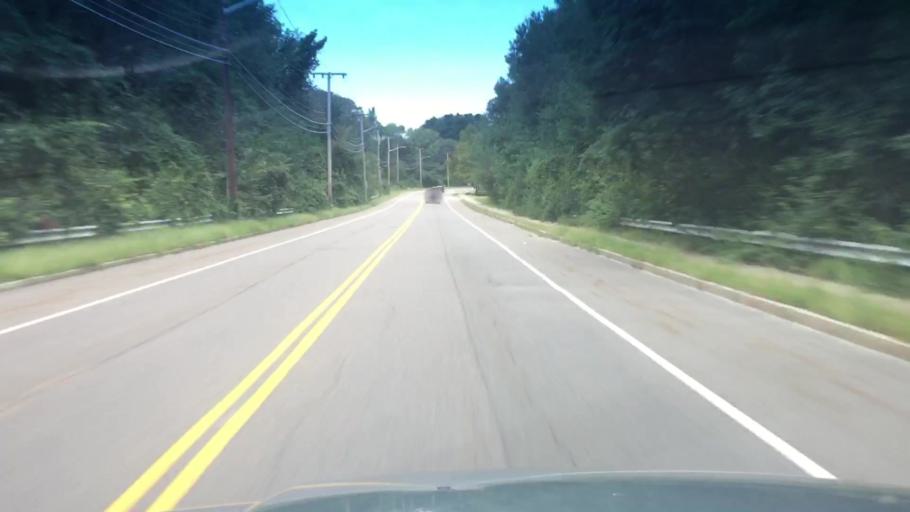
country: US
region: Massachusetts
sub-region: Norfolk County
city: Norwood
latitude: 42.2039
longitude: -71.1776
